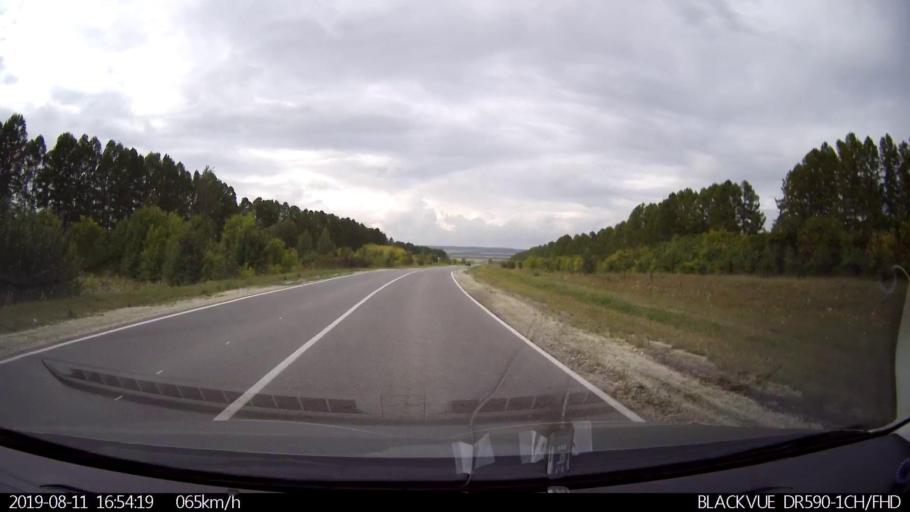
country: RU
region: Ulyanovsk
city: Mayna
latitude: 54.2714
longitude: 47.6664
